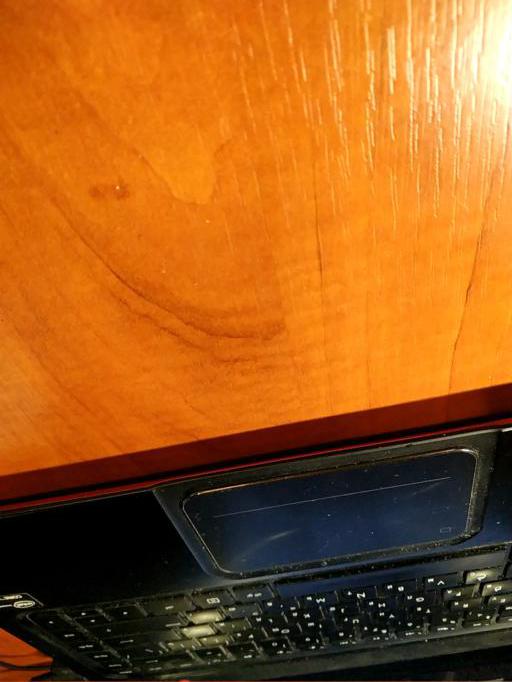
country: RU
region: Tverskaya
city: Zubtsov
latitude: 56.1577
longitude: 34.6394
